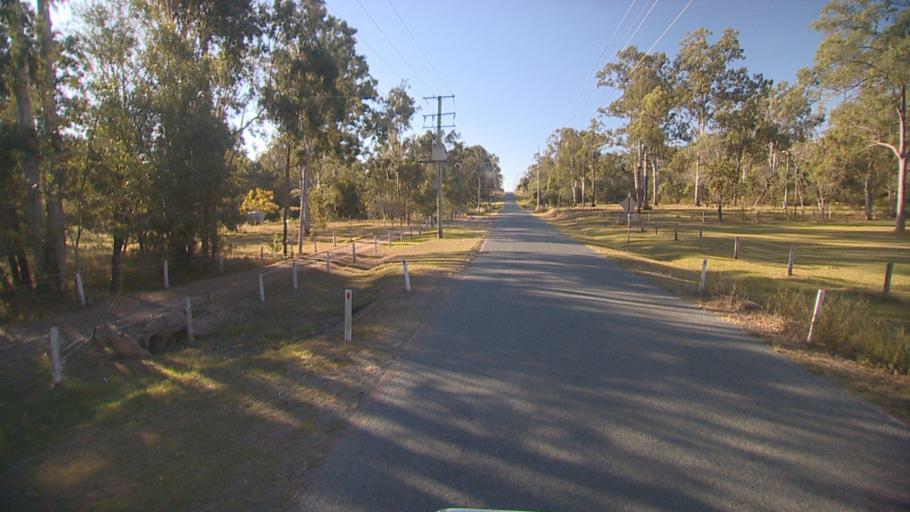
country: AU
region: Queensland
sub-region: Logan
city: North Maclean
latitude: -27.8030
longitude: 153.0407
